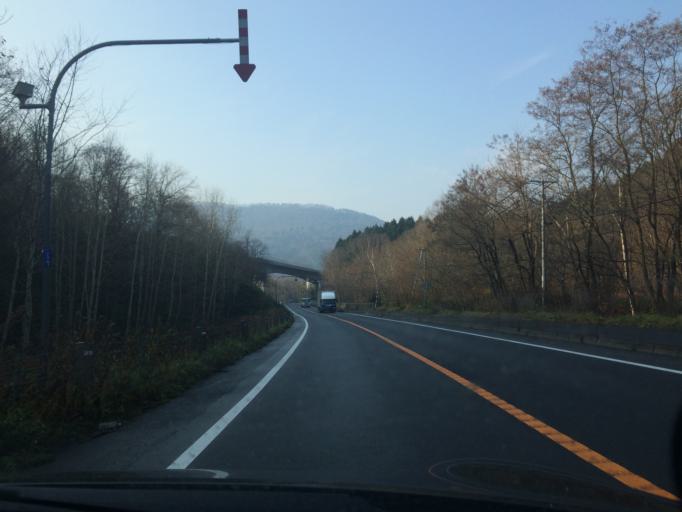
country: JP
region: Hokkaido
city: Iwamizawa
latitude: 42.9329
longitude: 142.0734
